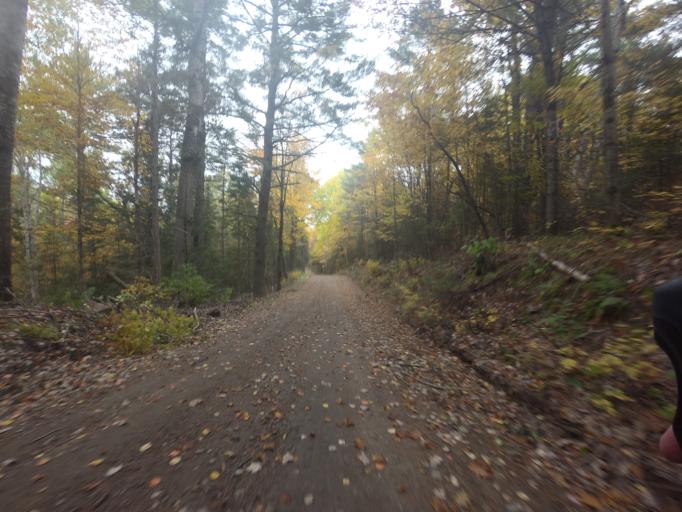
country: CA
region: Ontario
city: Petawawa
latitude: 45.7516
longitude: -77.2702
